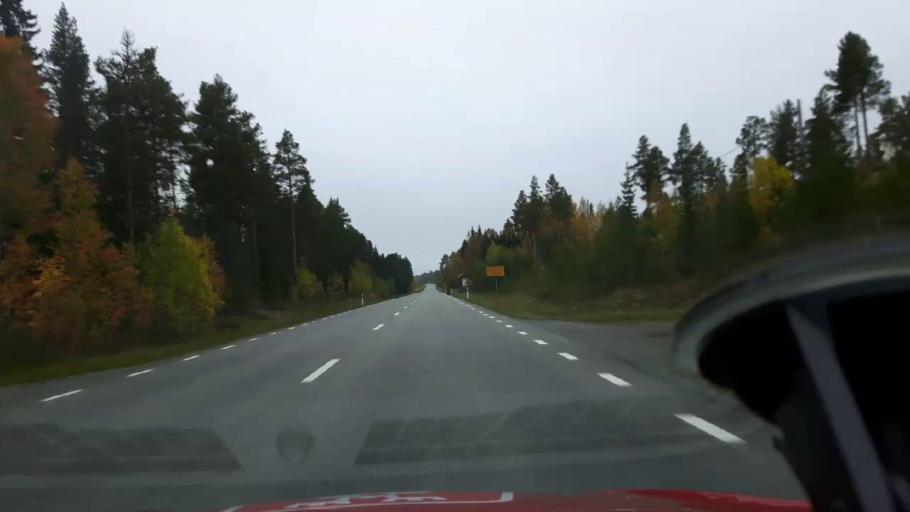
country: SE
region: Jaemtland
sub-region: Bergs Kommun
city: Hoverberg
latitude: 62.6706
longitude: 14.3821
